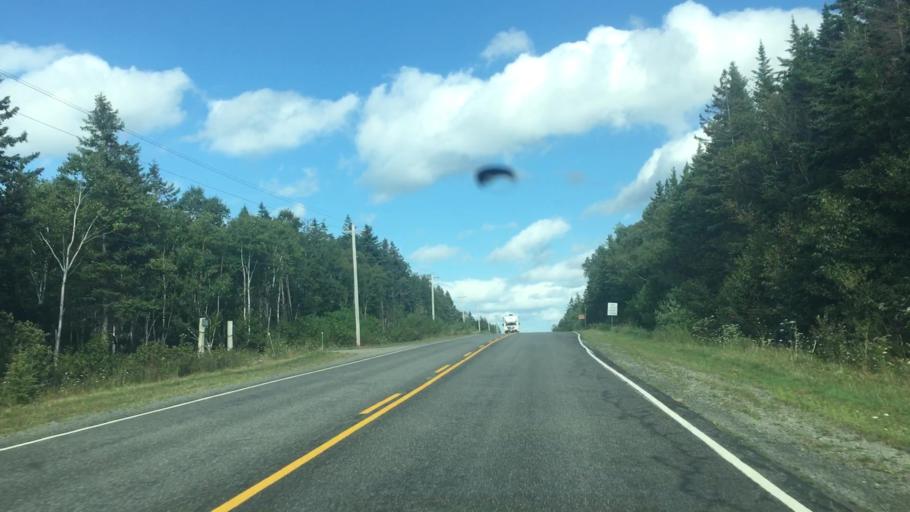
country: CA
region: Nova Scotia
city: Princeville
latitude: 45.8129
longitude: -60.7010
